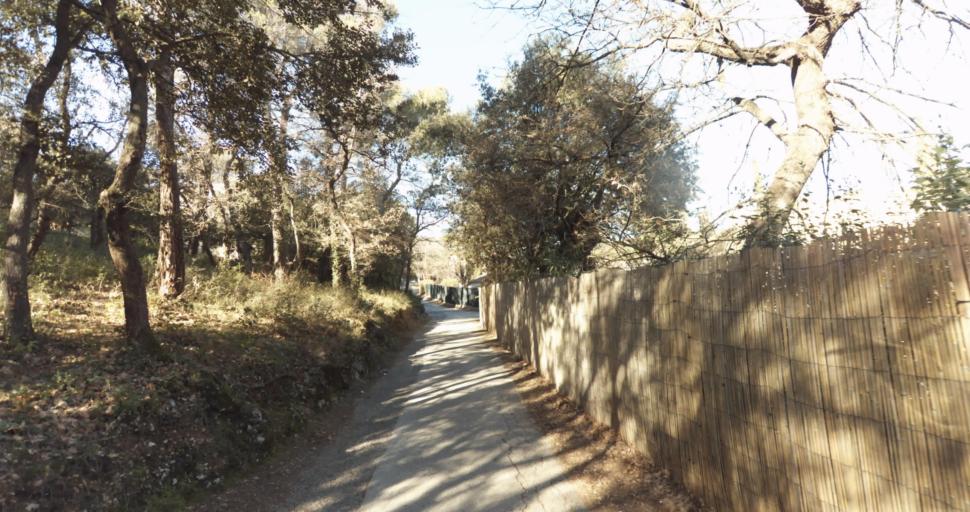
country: FR
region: Provence-Alpes-Cote d'Azur
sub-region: Departement des Bouches-du-Rhone
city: Peypin
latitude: 43.3831
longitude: 5.5852
